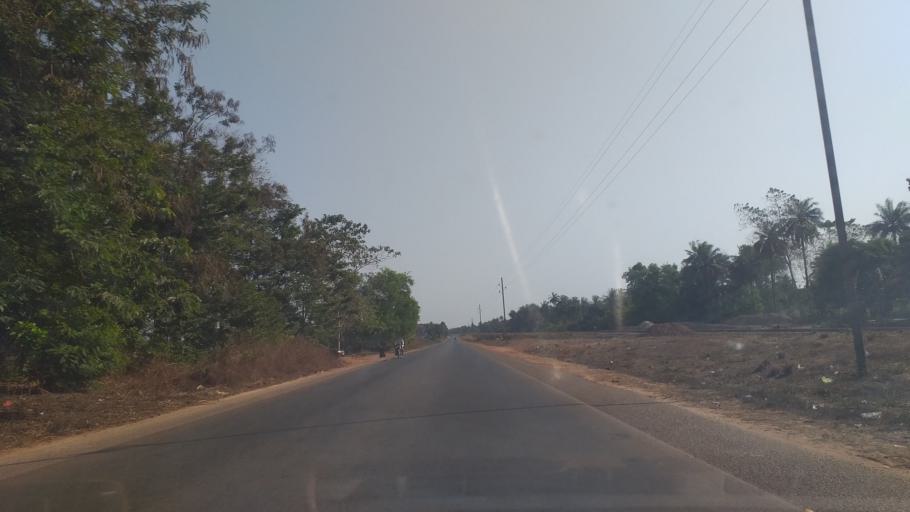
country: GN
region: Boke
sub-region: Boke Prefecture
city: Kamsar
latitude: 10.7457
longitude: -14.5103
